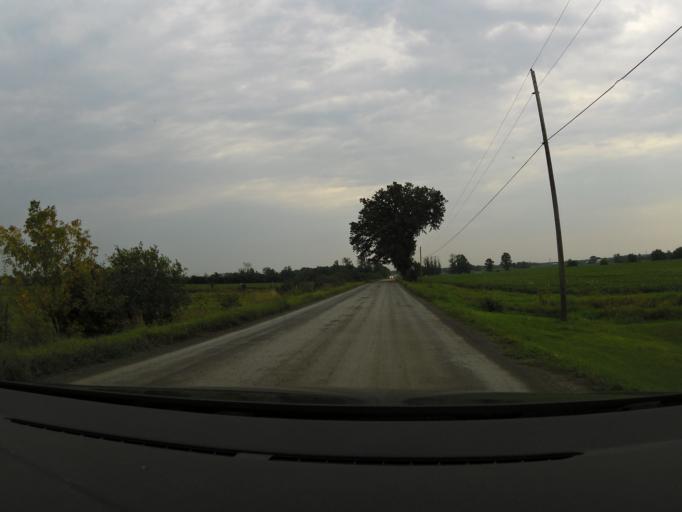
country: CA
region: Ontario
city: Carleton Place
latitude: 45.2230
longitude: -76.1730
